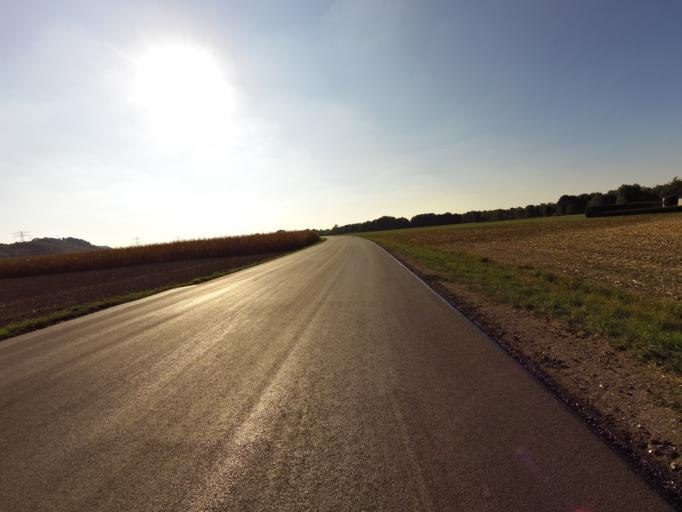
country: DE
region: Bavaria
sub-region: Lower Bavaria
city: Stallwang
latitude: 48.5862
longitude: 12.2542
